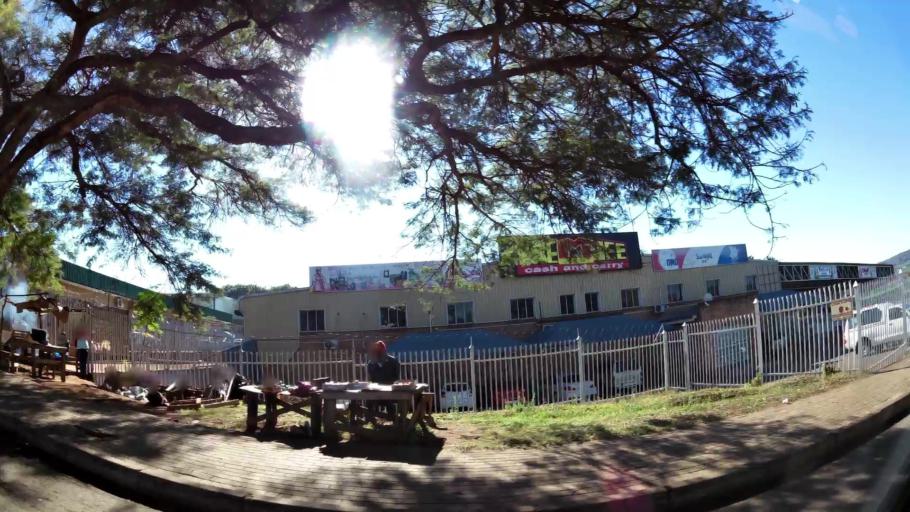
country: ZA
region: Limpopo
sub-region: Mopani District Municipality
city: Tzaneen
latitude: -23.8347
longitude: 30.1702
